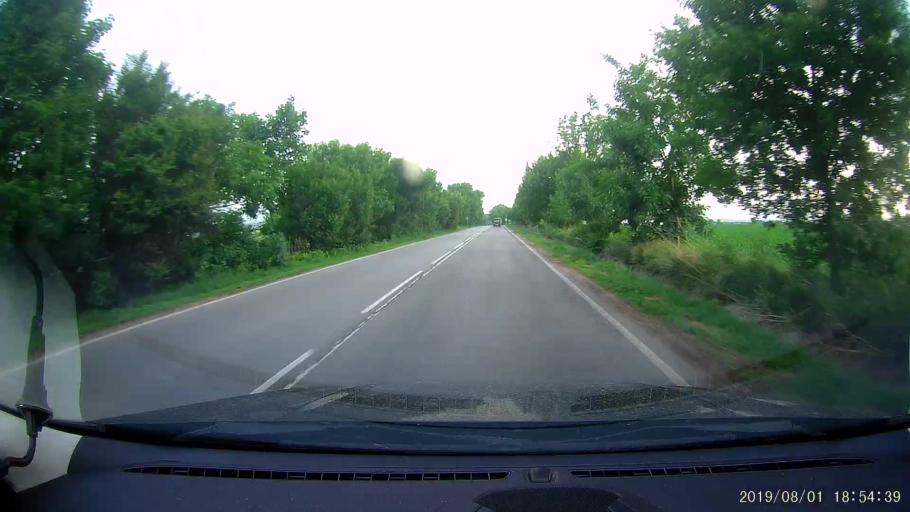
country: BG
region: Shumen
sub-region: Obshtina Shumen
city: Shumen
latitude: 43.1934
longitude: 27.0028
